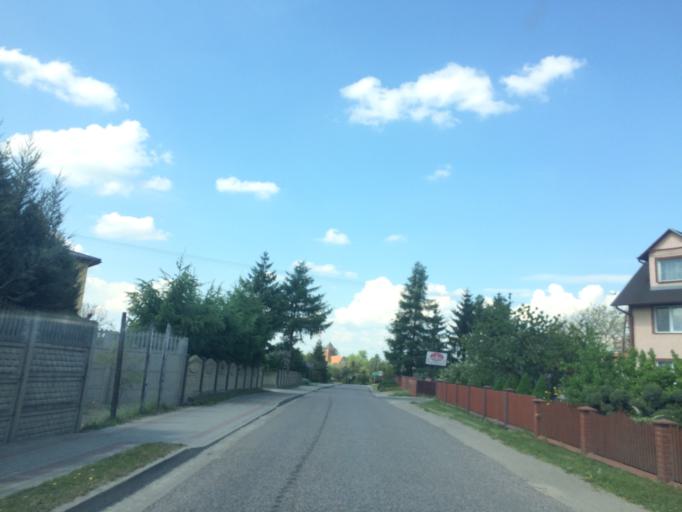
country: PL
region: Warmian-Masurian Voivodeship
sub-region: Powiat ilawski
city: Lubawa
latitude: 53.4124
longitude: 19.7670
